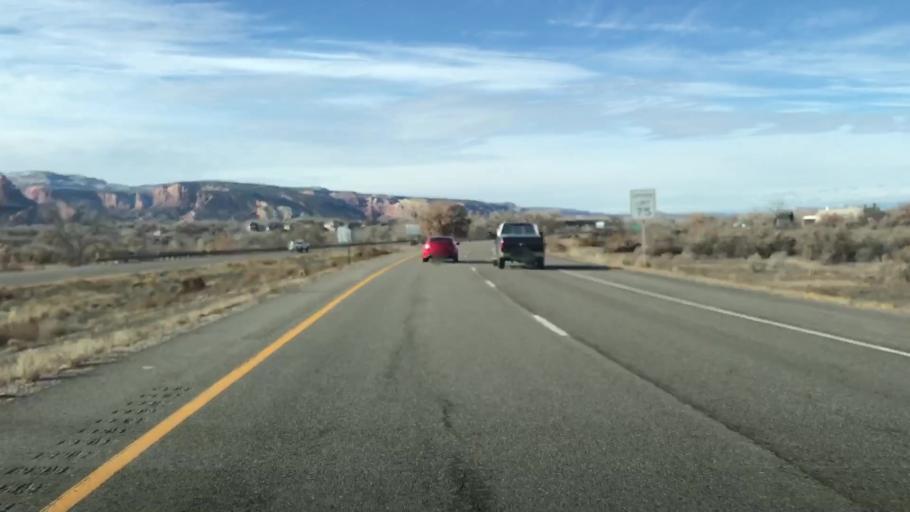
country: US
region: Colorado
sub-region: Mesa County
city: Redlands
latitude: 39.1094
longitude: -108.6544
